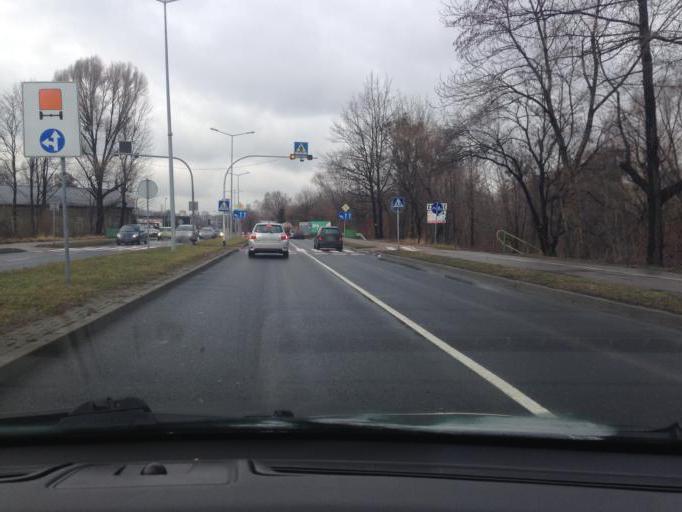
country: PL
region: Silesian Voivodeship
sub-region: Bielsko-Biala
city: Bielsko-Biala
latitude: 49.7969
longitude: 19.0544
